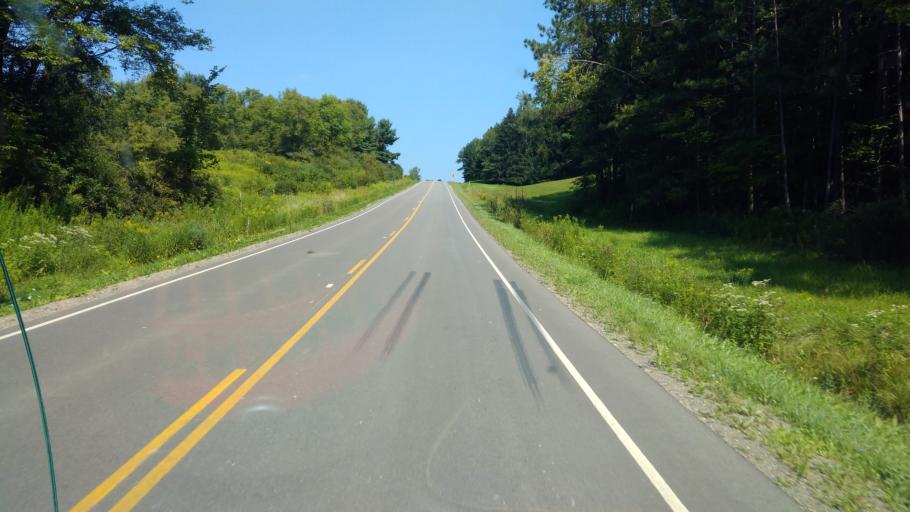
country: US
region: New York
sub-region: Allegany County
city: Belmont
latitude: 42.2678
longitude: -78.0425
